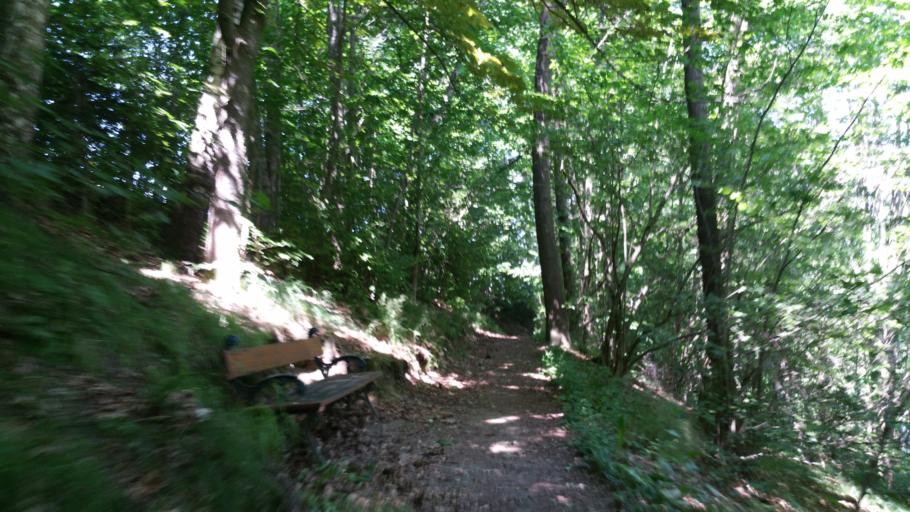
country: DE
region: Bavaria
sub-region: Upper Franconia
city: Schwarzenbach an der Saale
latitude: 50.2310
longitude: 11.9344
